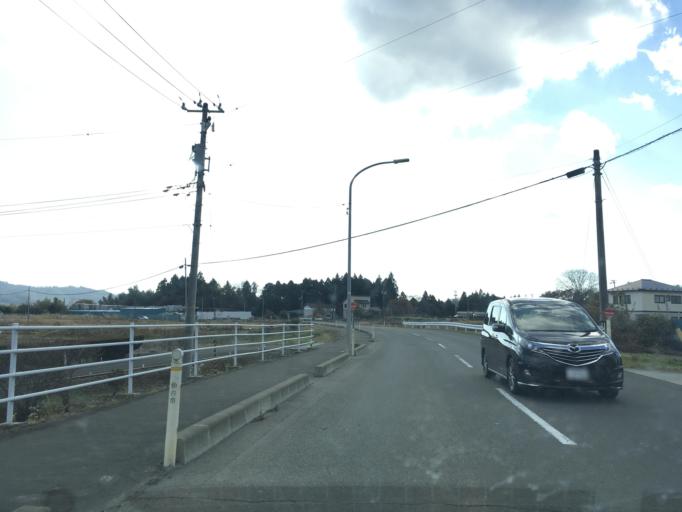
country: JP
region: Miyagi
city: Sendai
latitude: 38.2831
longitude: 140.7570
